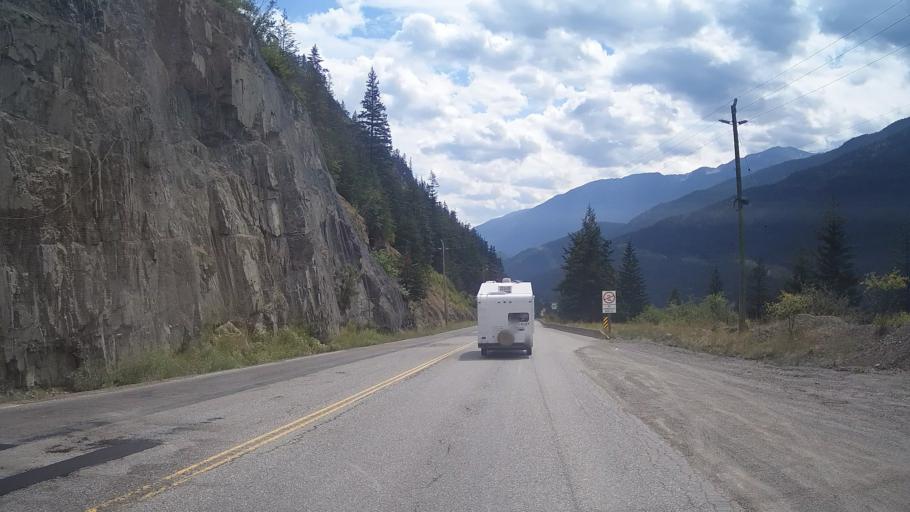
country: CA
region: British Columbia
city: Hope
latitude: 50.0752
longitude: -121.5471
